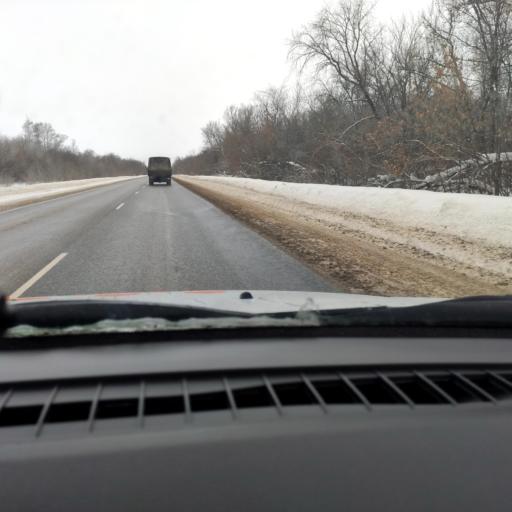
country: RU
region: Samara
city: Dubovyy Umet
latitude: 52.9584
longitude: 50.2974
